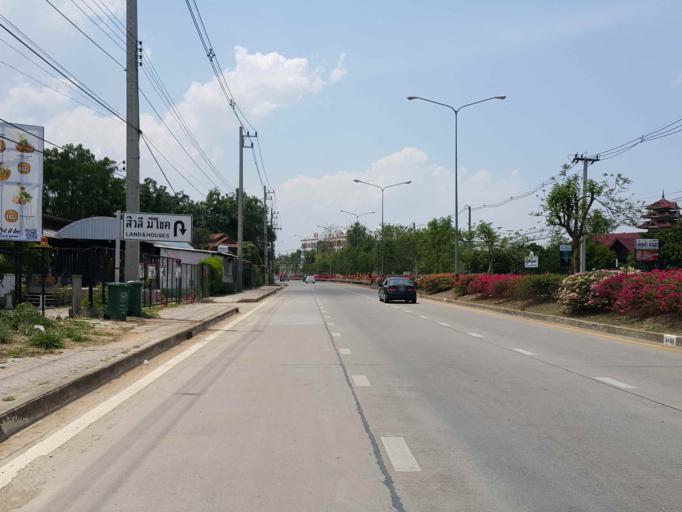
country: TH
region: Chiang Mai
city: San Sai
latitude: 18.8440
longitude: 98.9955
